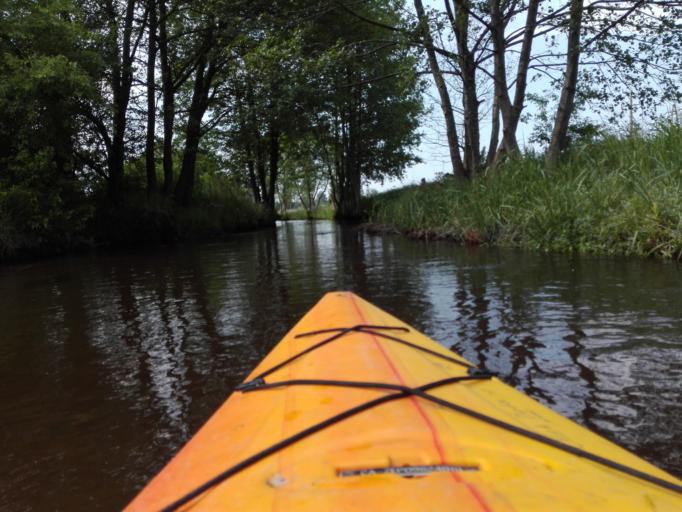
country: PL
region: West Pomeranian Voivodeship
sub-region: Powiat koszalinski
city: Sianow
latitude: 54.2173
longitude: 16.3040
